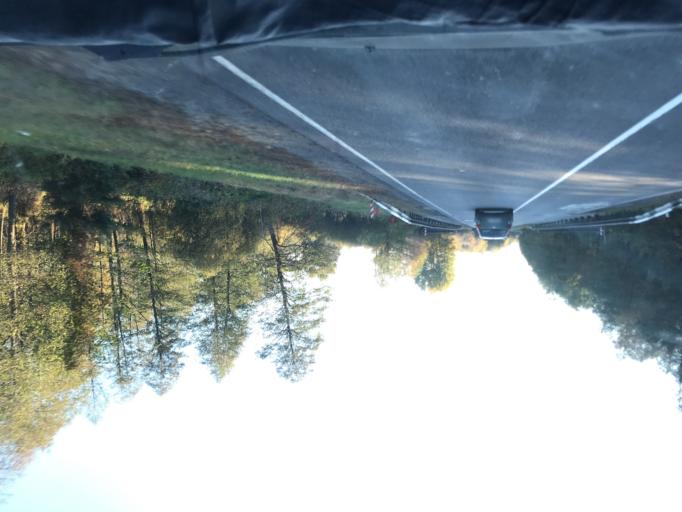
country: BY
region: Gomel
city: Pyetrykaw
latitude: 52.2745
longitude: 28.2484
